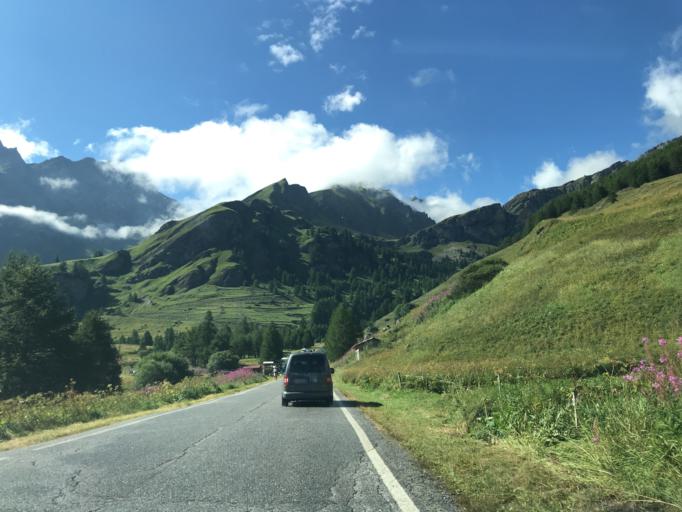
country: IT
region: Piedmont
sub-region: Provincia di Cuneo
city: Pontechianale
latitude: 44.6489
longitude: 6.9966
